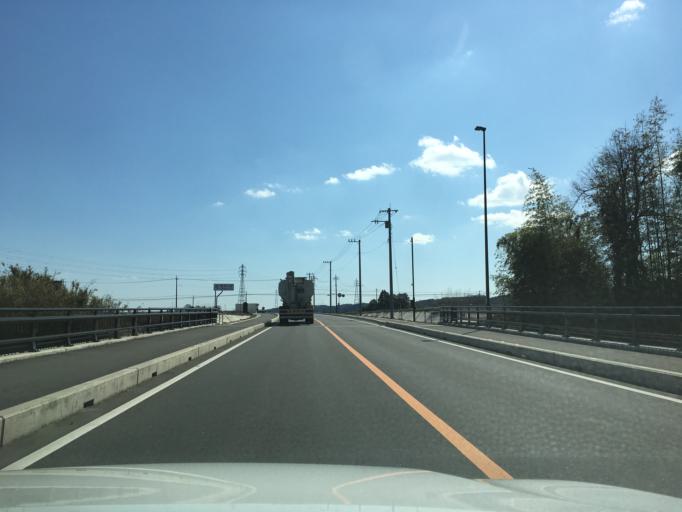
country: JP
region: Tochigi
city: Otawara
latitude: 36.7847
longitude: 140.1168
